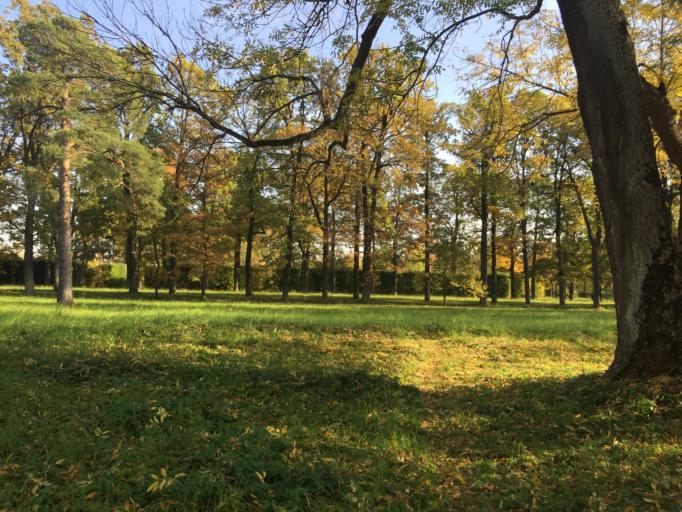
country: RU
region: St.-Petersburg
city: Pushkin
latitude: 59.7174
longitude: 30.3866
